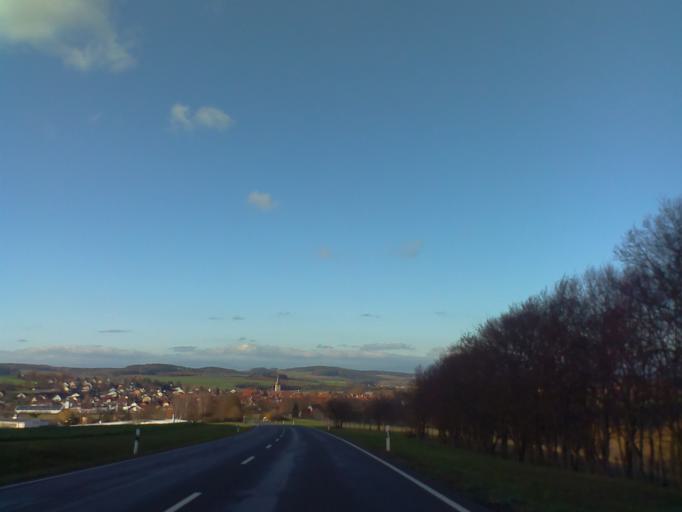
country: DE
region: Bavaria
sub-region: Regierungsbezirk Unterfranken
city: Saal an der Saale
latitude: 50.3132
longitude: 10.3745
